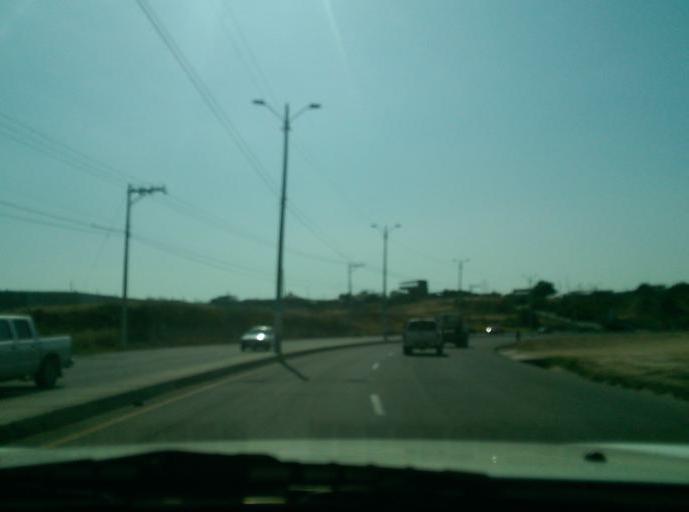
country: EC
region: Manabi
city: Manta
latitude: -0.9801
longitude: -80.7205
